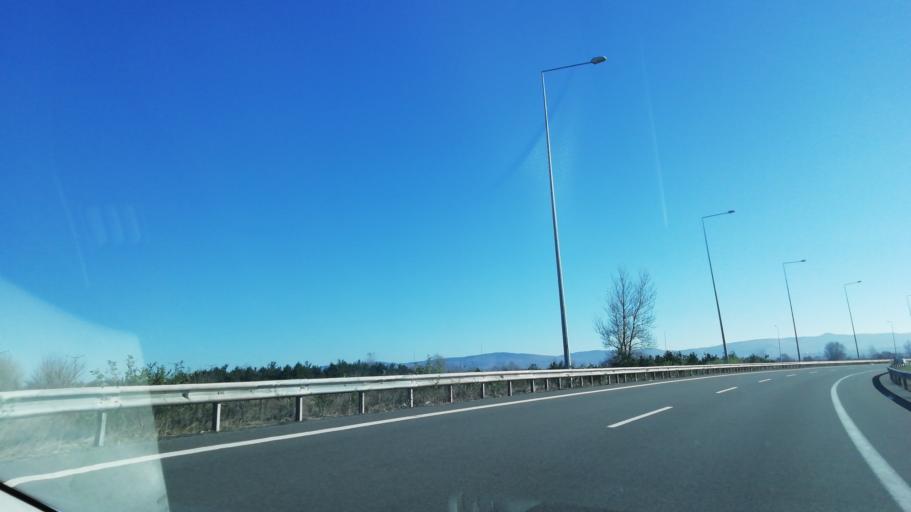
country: TR
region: Bolu
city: Gerede
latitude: 40.7383
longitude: 32.1836
